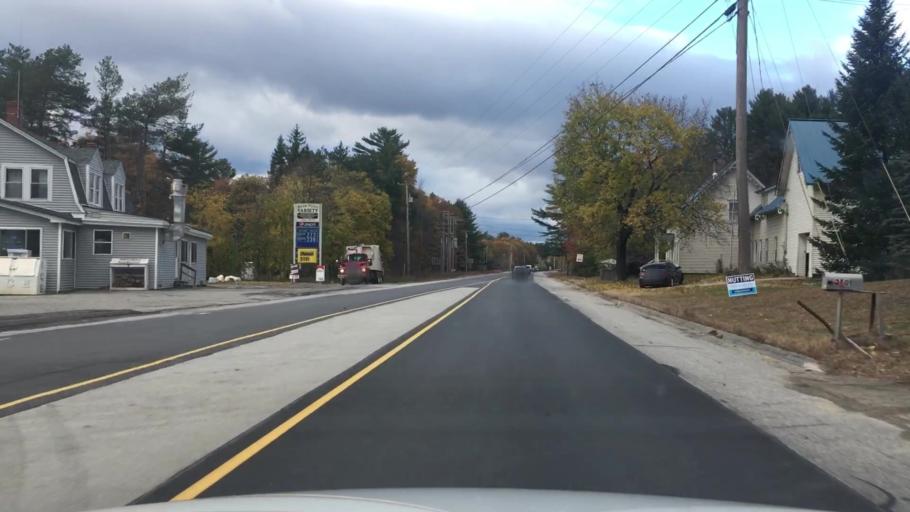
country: US
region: Maine
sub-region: Androscoggin County
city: Livermore
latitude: 44.3439
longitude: -70.2565
